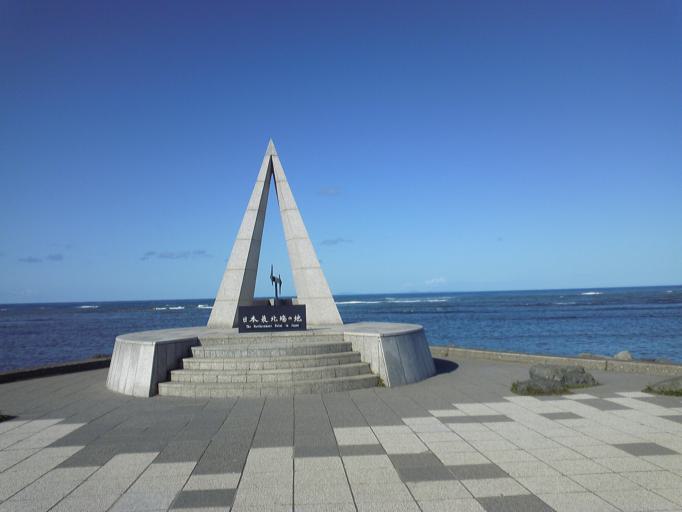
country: JP
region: Hokkaido
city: Makubetsu
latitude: 45.5226
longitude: 141.9366
